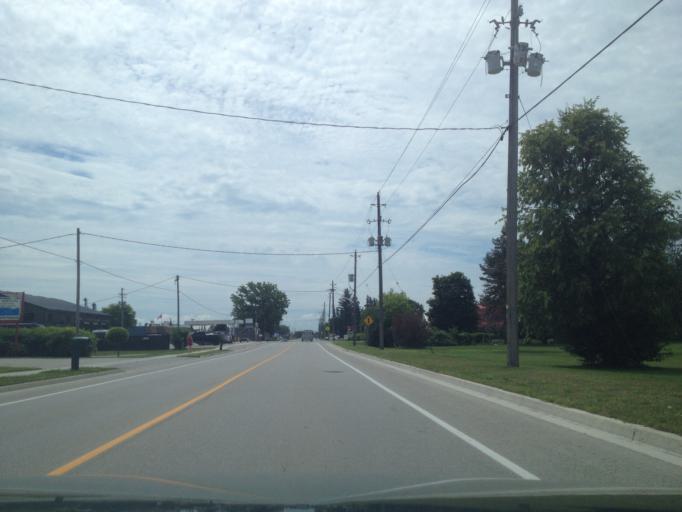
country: CA
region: Ontario
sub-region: Oxford County
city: Woodstock
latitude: 42.9807
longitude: -80.5956
